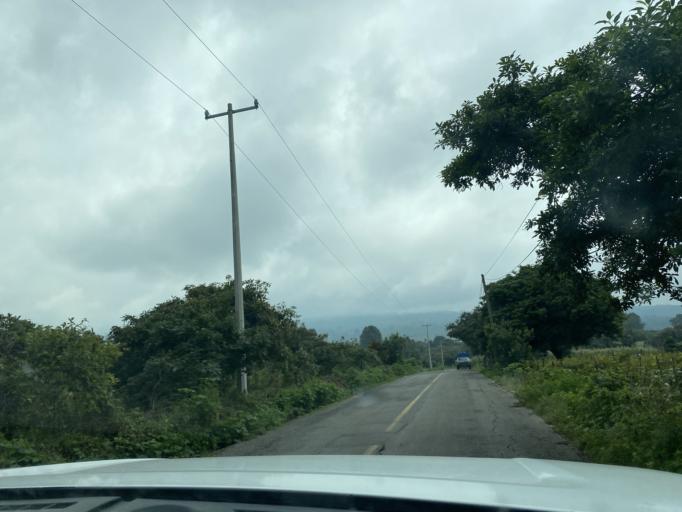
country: MX
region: Morelos
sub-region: Yecapixtla
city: Texcala
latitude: 18.9333
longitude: -98.8063
